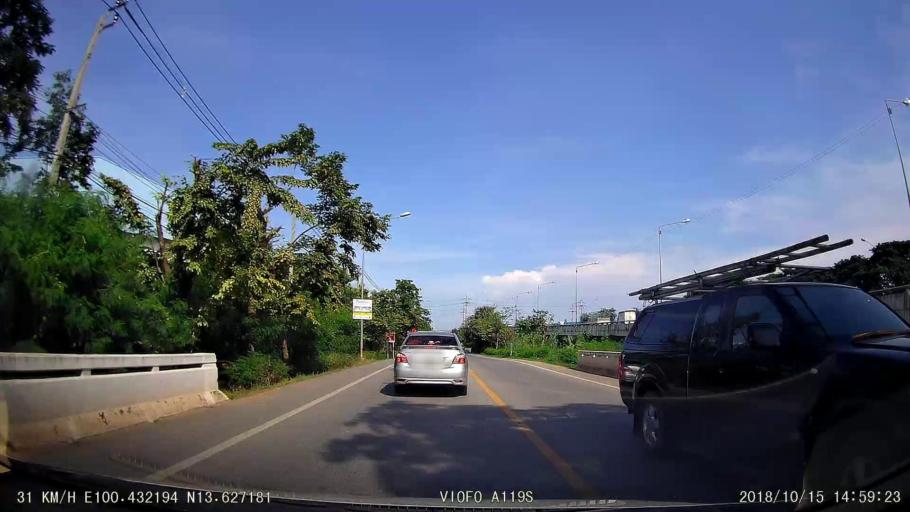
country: TH
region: Bangkok
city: Bang Khun Thian
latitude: 13.6272
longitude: 100.4321
